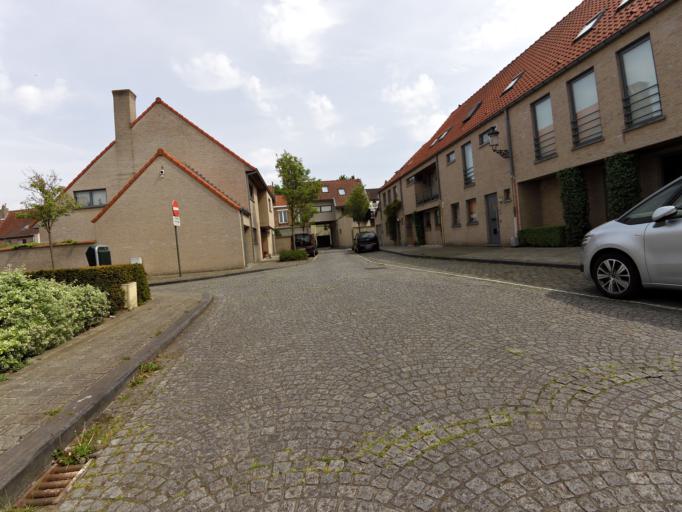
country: BE
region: Flanders
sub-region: Provincie West-Vlaanderen
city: Brugge
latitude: 51.2176
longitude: 3.2228
